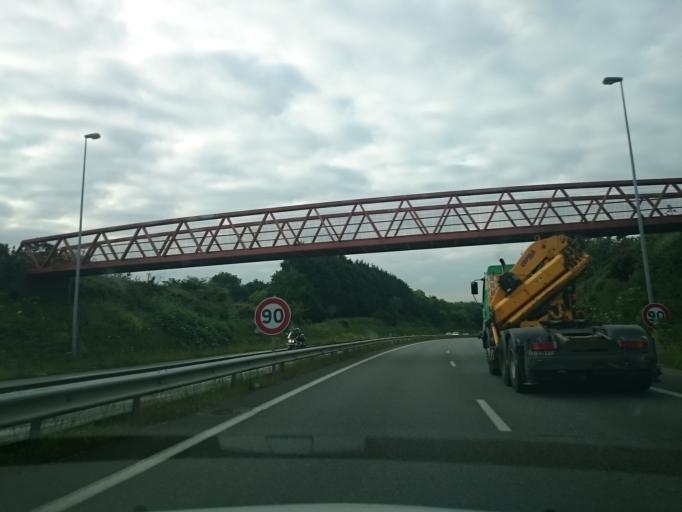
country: FR
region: Brittany
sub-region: Departement du Finistere
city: Le Relecq-Kerhuon
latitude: 48.4104
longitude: -4.4166
